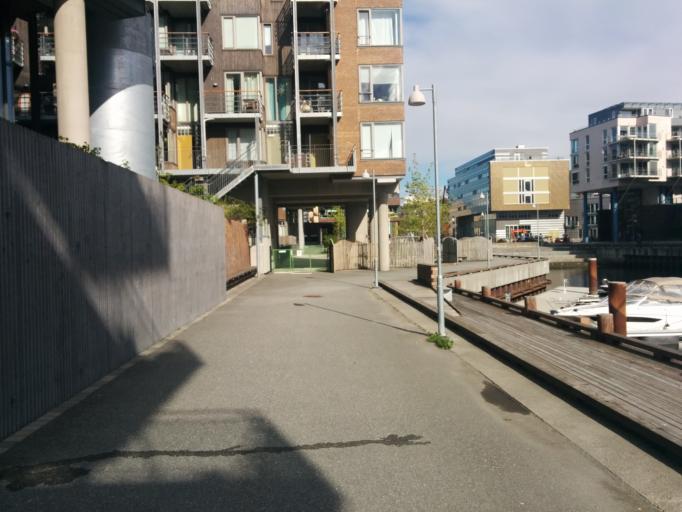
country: NO
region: Sor-Trondelag
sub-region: Trondheim
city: Trondheim
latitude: 63.4361
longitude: 10.4126
